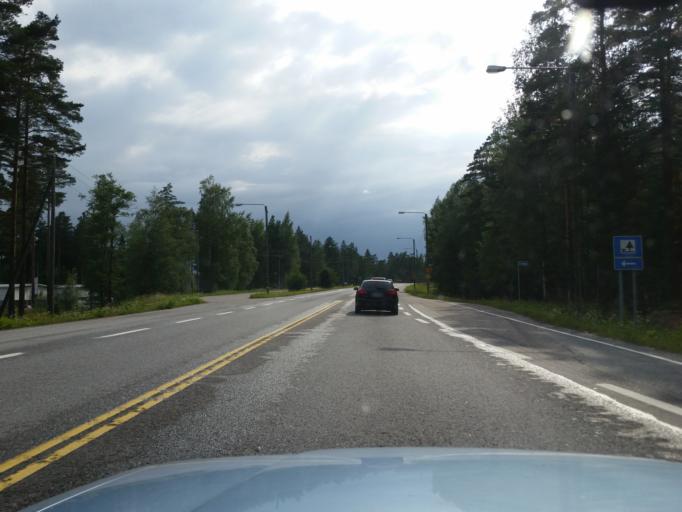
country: FI
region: Uusimaa
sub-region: Raaseporin
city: Pohja
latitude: 60.0081
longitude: 23.5423
